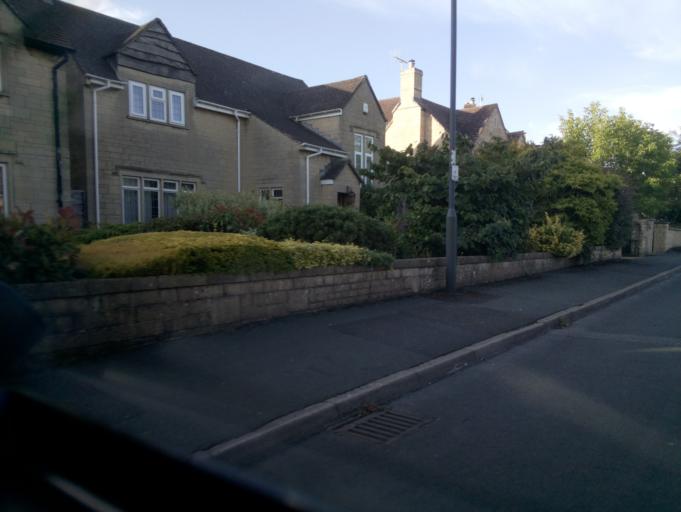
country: GB
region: England
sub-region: South Gloucestershire
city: Mangotsfield
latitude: 51.5010
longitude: -2.5143
